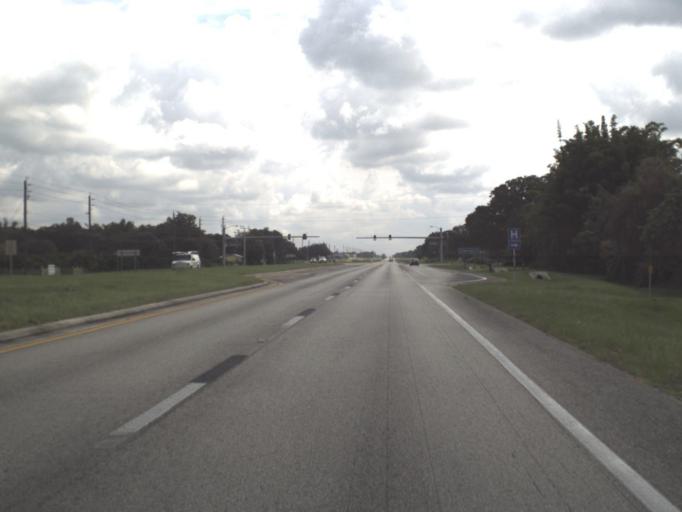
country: US
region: Florida
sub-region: Lee County
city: Alva
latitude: 26.7088
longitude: -81.6034
